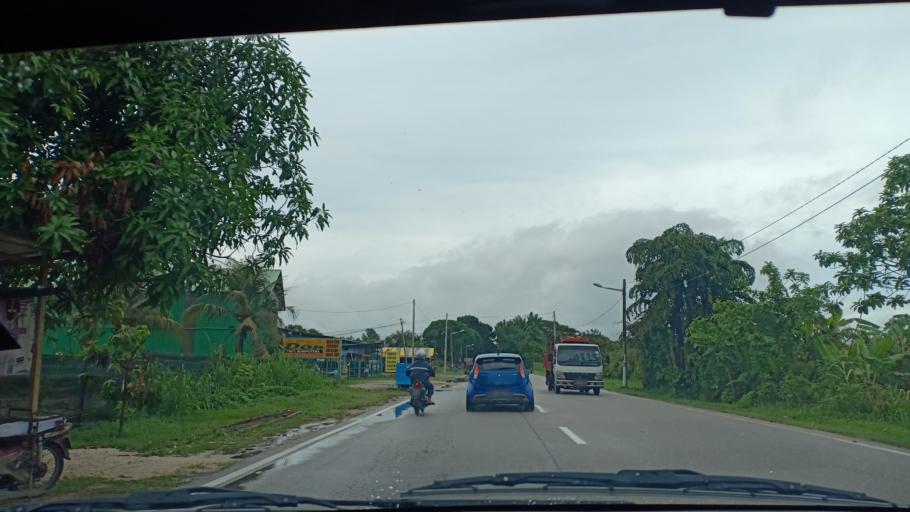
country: MY
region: Penang
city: Kepala Batas
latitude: 5.4928
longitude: 100.4548
